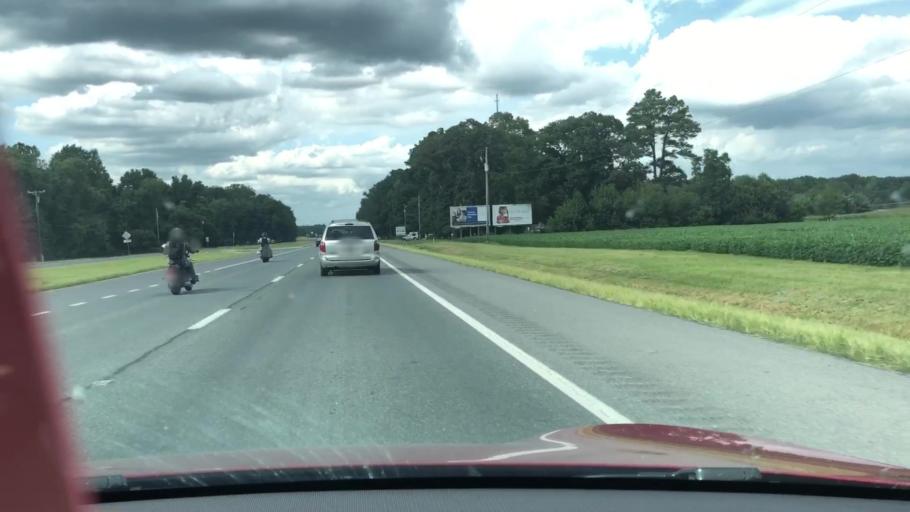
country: US
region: Delaware
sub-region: Sussex County
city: Delmar
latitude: 38.5030
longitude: -75.5571
